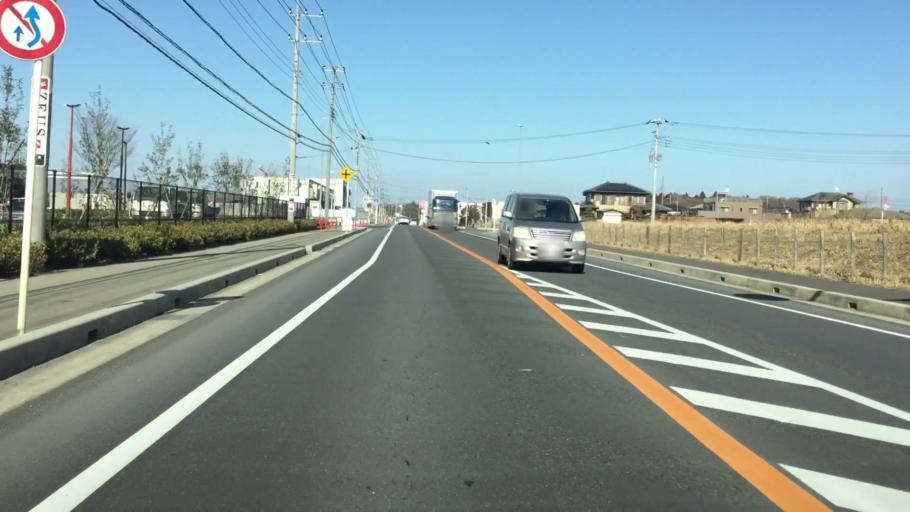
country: JP
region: Chiba
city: Shiroi
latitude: 35.8160
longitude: 140.1342
